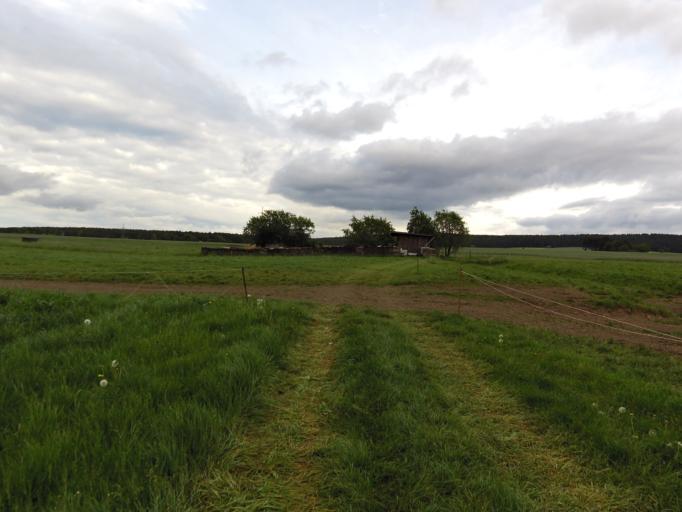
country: DE
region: Thuringia
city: Frauensee
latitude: 50.9192
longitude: 10.1007
